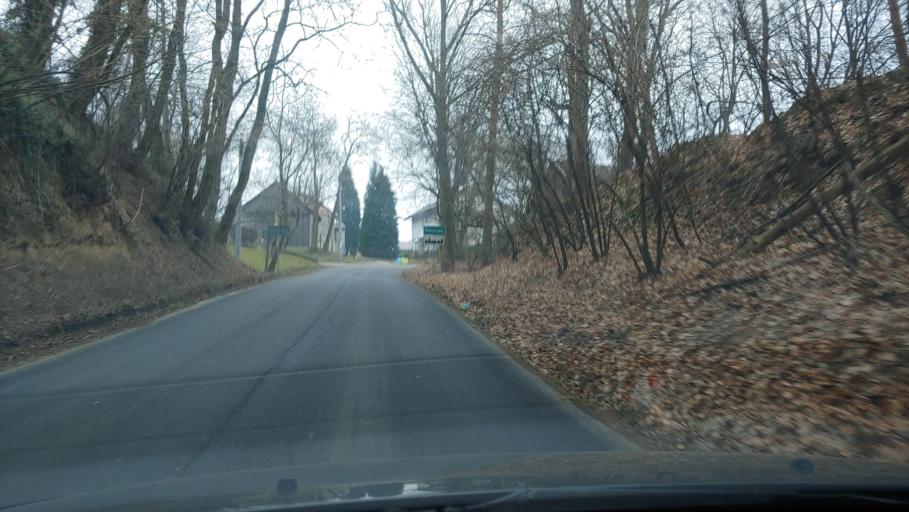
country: PL
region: Lesser Poland Voivodeship
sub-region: Powiat krakowski
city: Rudawa
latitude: 50.1065
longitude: 19.7495
